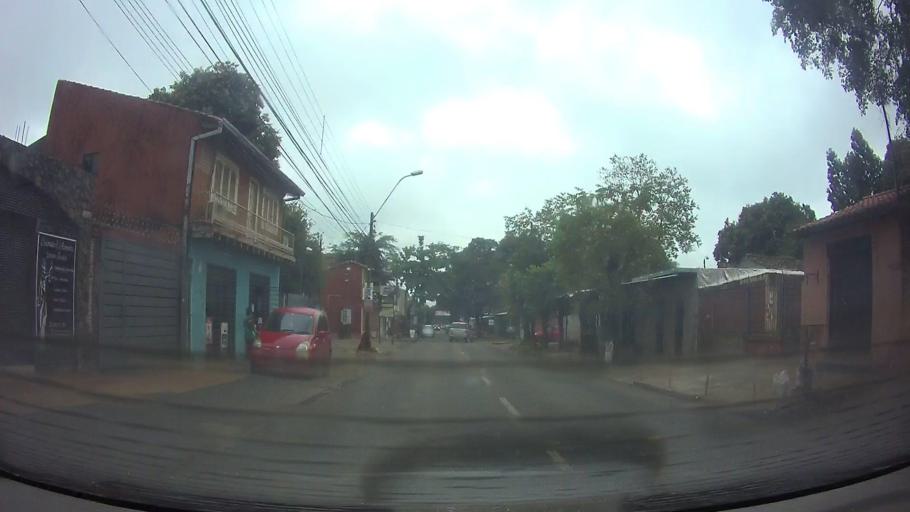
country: PY
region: Central
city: Fernando de la Mora
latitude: -25.3348
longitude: -57.5605
